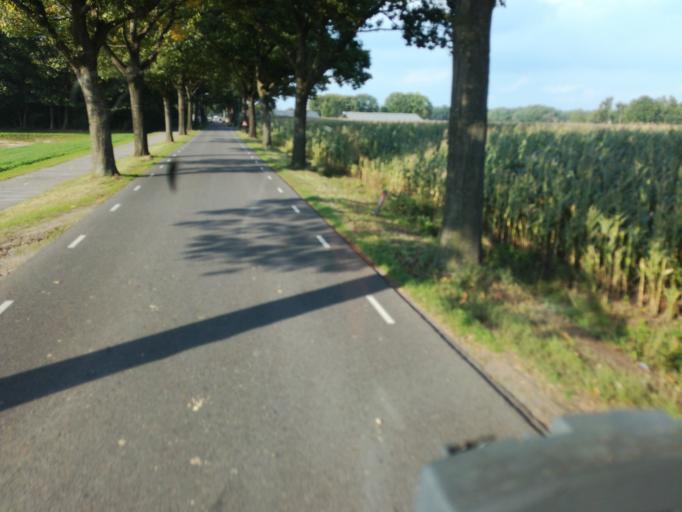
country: NL
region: North Brabant
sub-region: Gemeente Uden
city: Volkel
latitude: 51.6651
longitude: 5.6733
